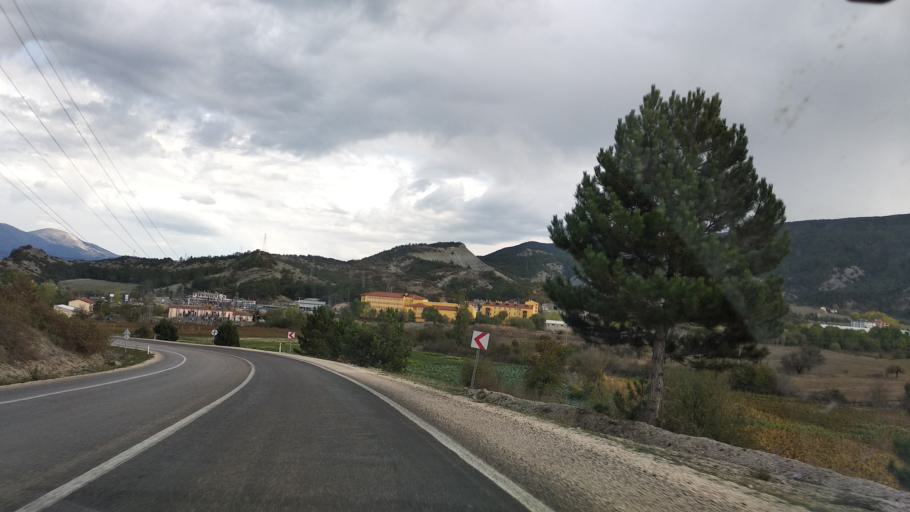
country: TR
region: Bolu
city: Mudurnu
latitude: 40.4866
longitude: 31.1955
